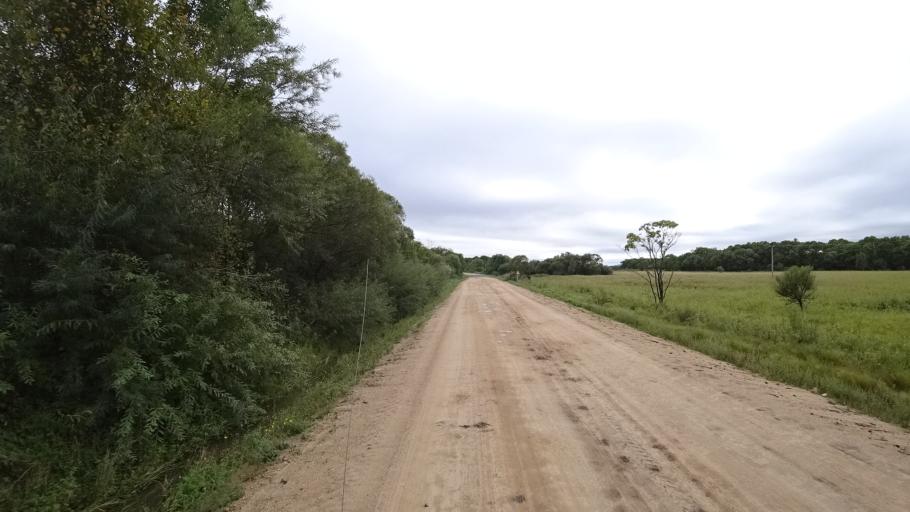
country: RU
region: Primorskiy
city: Monastyrishche
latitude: 44.1009
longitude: 132.6051
